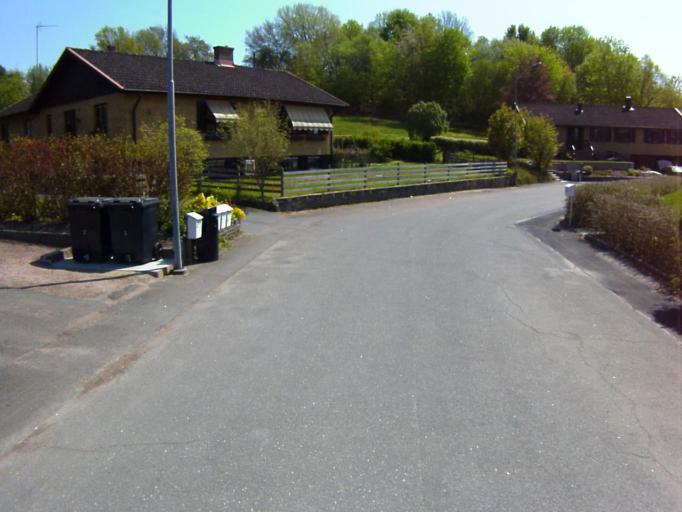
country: SE
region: Skane
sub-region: Kristianstads Kommun
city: Tollarp
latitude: 56.1677
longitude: 14.2923
